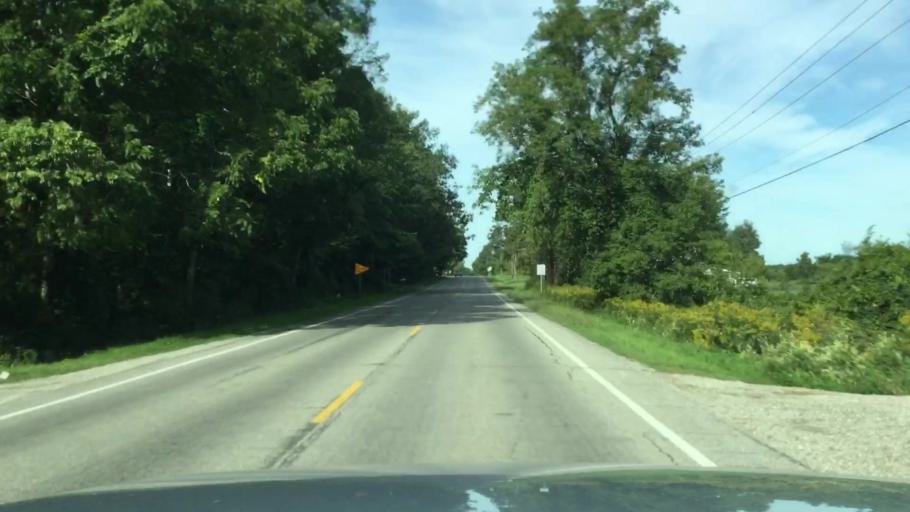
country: US
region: Michigan
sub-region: Genesee County
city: Flushing
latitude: 43.1178
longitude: -83.8776
